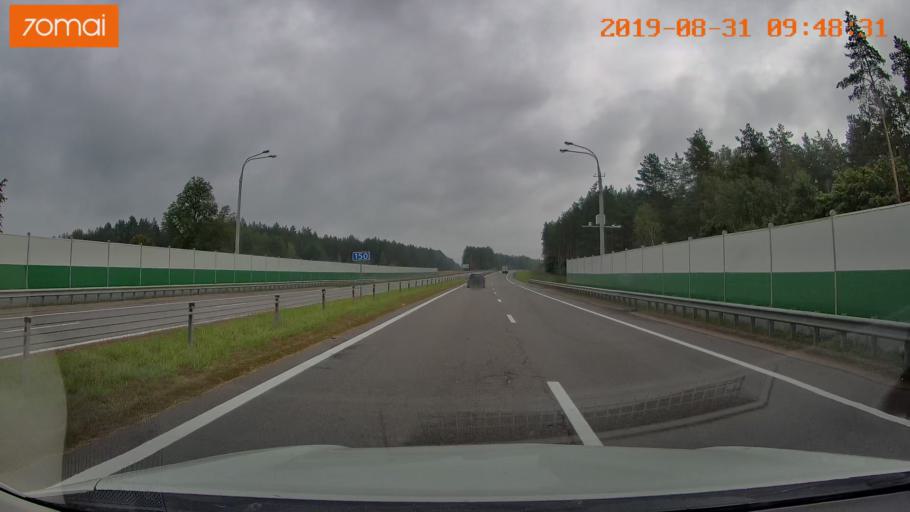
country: BY
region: Mogilev
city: Byalynichy
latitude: 53.9588
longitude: 29.6613
